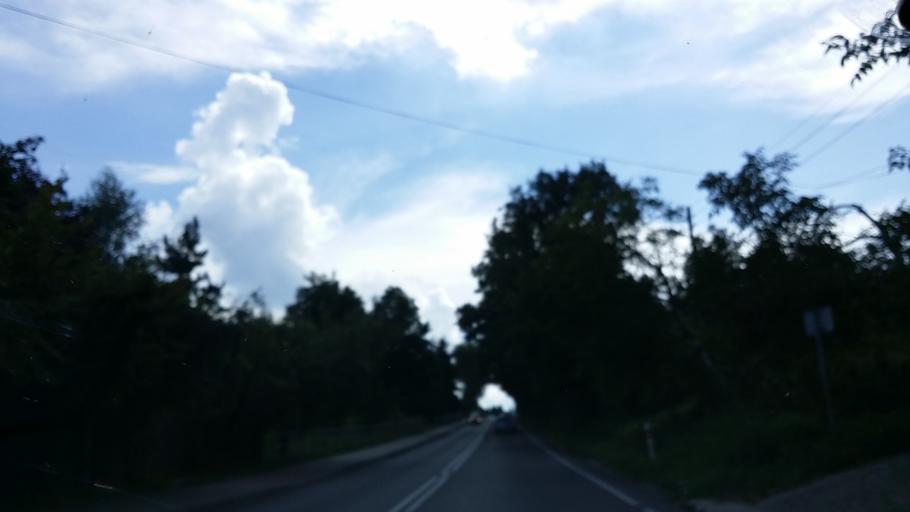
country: PL
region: Lesser Poland Voivodeship
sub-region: Powiat wielicki
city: Wieliczka
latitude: 49.9749
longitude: 20.0639
